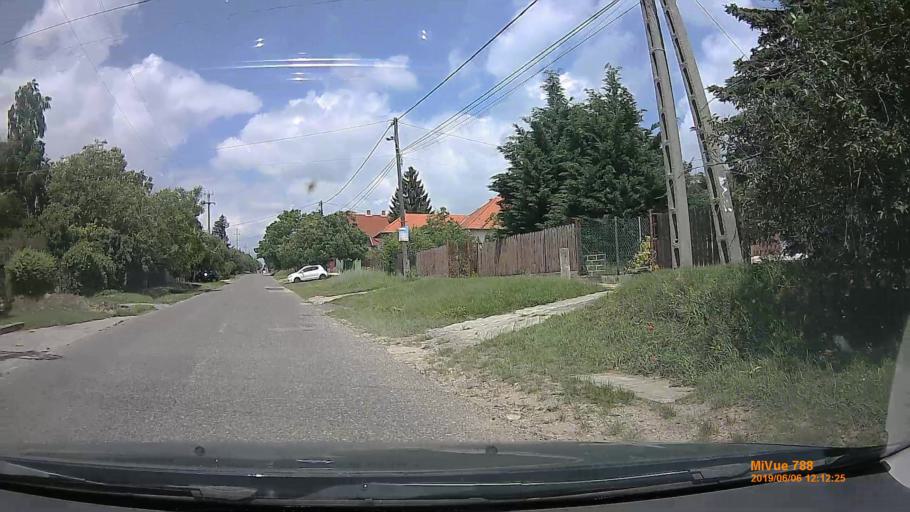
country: HU
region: Pest
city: Kerepes
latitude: 47.5754
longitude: 19.2659
